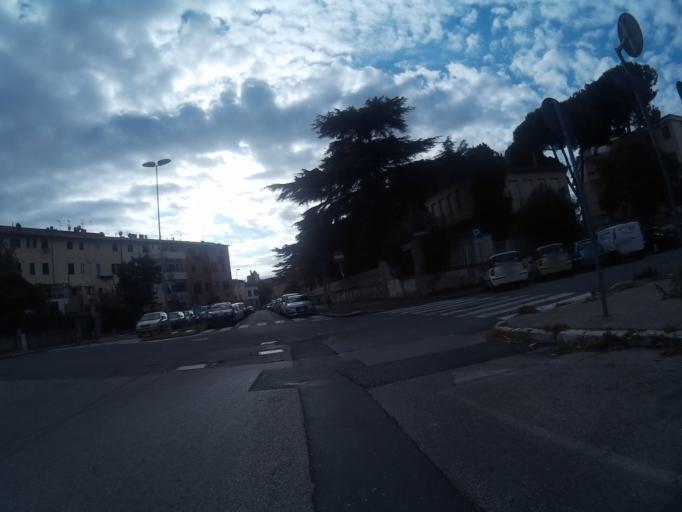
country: IT
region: Tuscany
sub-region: Provincia di Livorno
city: Livorno
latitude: 43.5580
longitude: 10.3201
